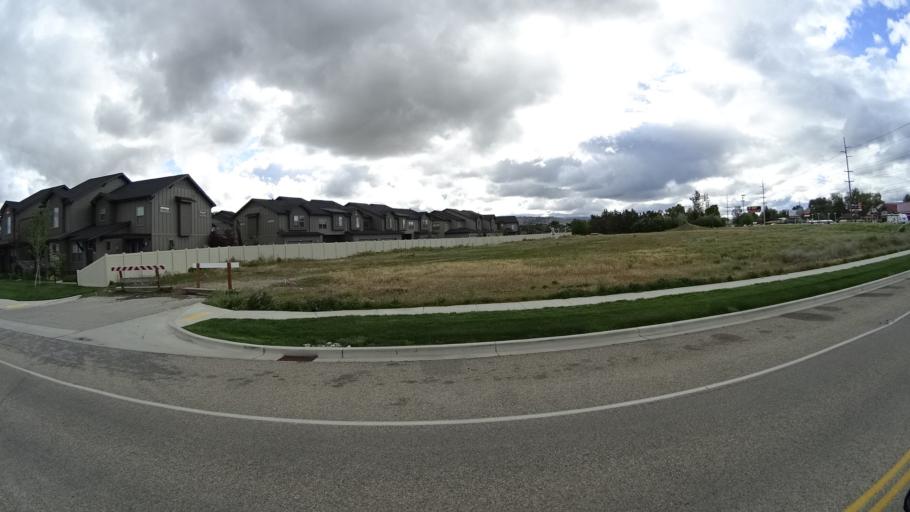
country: US
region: Idaho
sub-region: Ada County
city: Eagle
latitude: 43.6761
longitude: -116.2944
